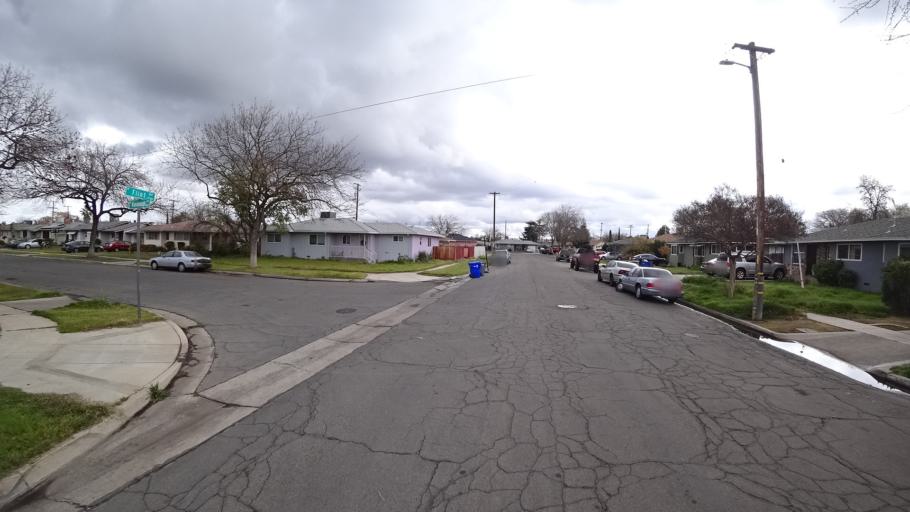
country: US
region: California
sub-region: Fresno County
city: Fresno
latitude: 36.7878
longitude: -119.8376
